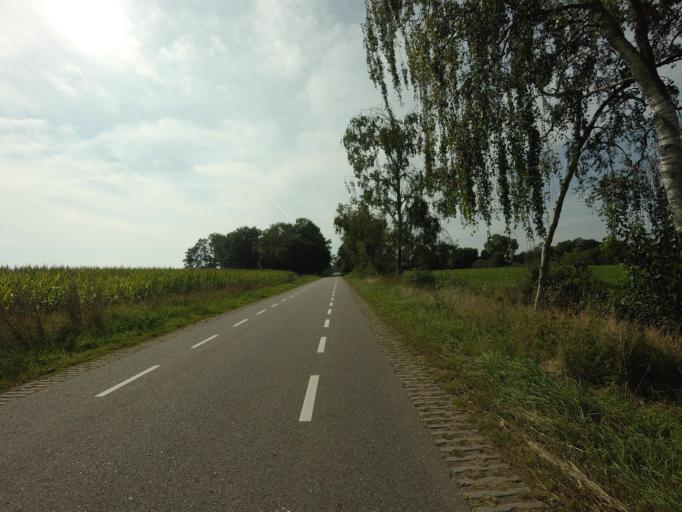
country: NL
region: Overijssel
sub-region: Gemeente Hof van Twente
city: Goor
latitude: 52.2627
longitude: 6.5575
